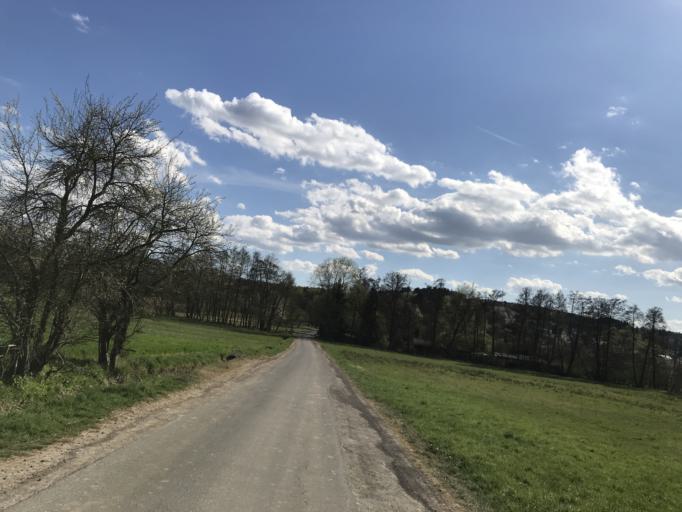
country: DE
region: Hesse
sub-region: Regierungsbezirk Giessen
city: Rabenau
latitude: 50.6777
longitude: 8.8321
